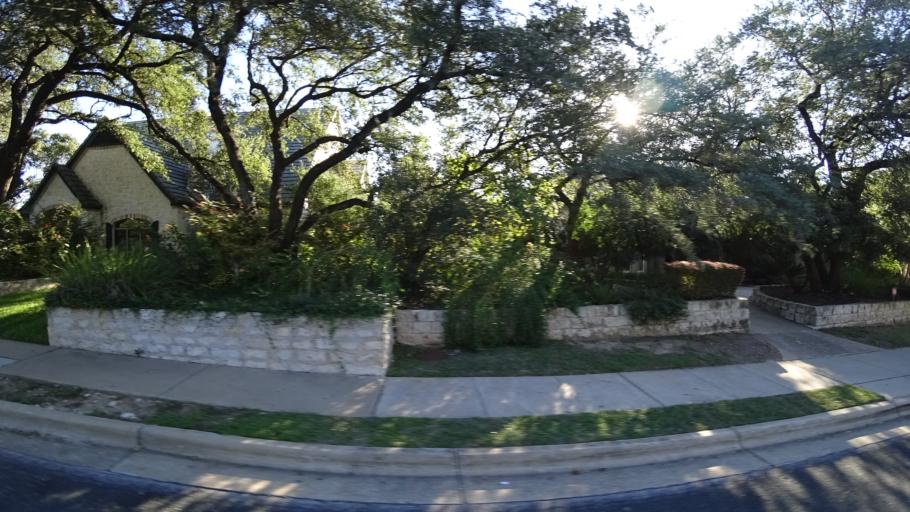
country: US
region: Texas
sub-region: Travis County
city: West Lake Hills
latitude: 30.3185
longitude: -97.8096
